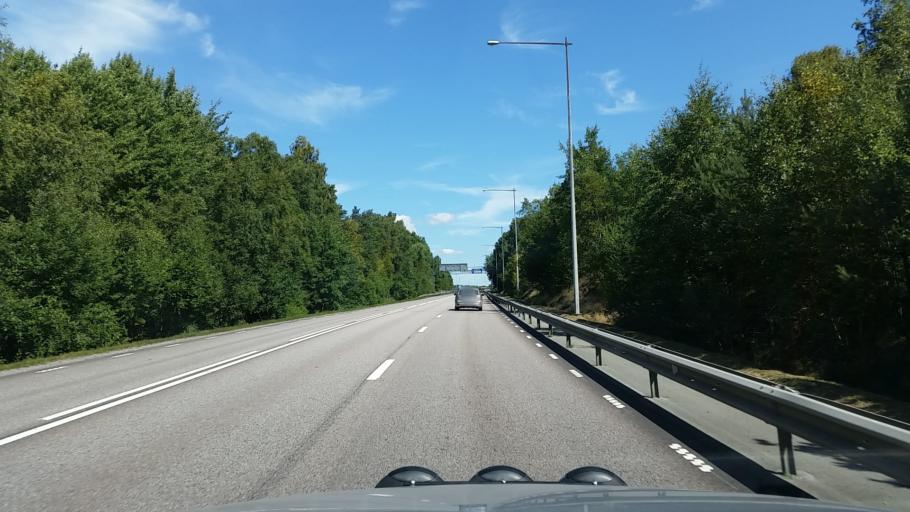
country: SE
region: Vaestra Goetaland
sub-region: Goteborg
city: Majorna
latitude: 57.7164
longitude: 11.8612
